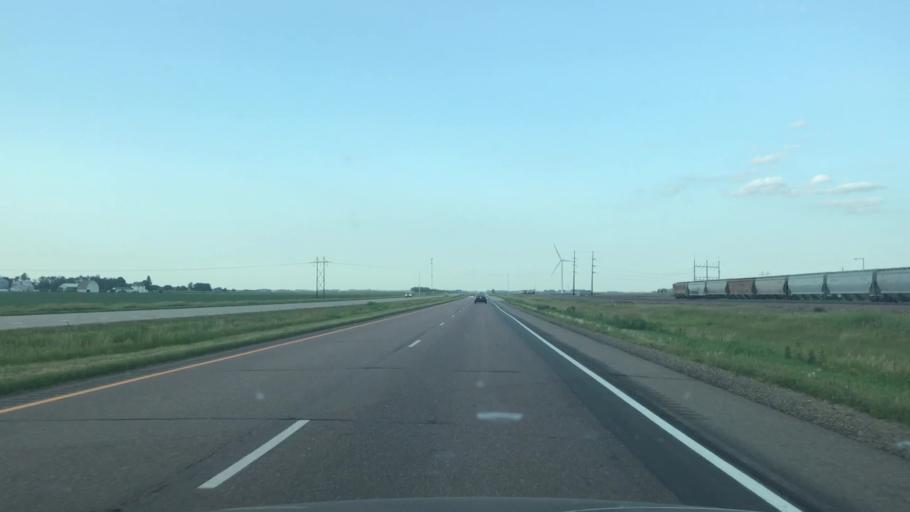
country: US
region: Minnesota
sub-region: Nobles County
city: Worthington
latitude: 43.7074
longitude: -95.4580
